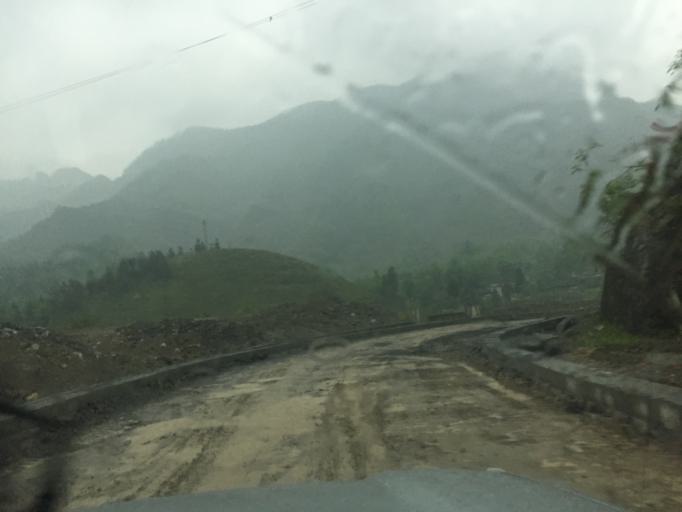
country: CN
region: Guizhou Sheng
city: Changfeng
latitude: 28.4300
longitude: 108.0796
